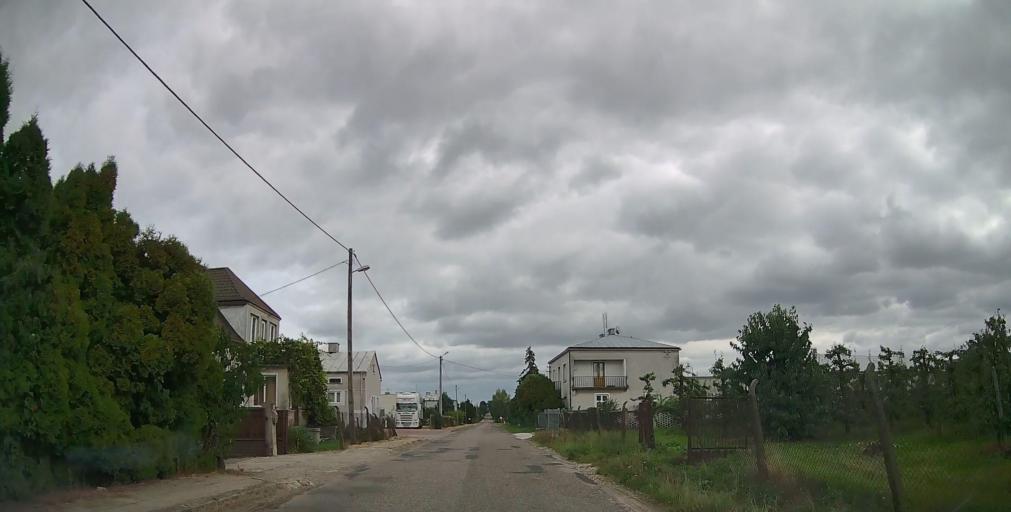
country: PL
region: Masovian Voivodeship
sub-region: Powiat grojecki
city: Belsk Duzy
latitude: 51.8242
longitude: 20.8125
